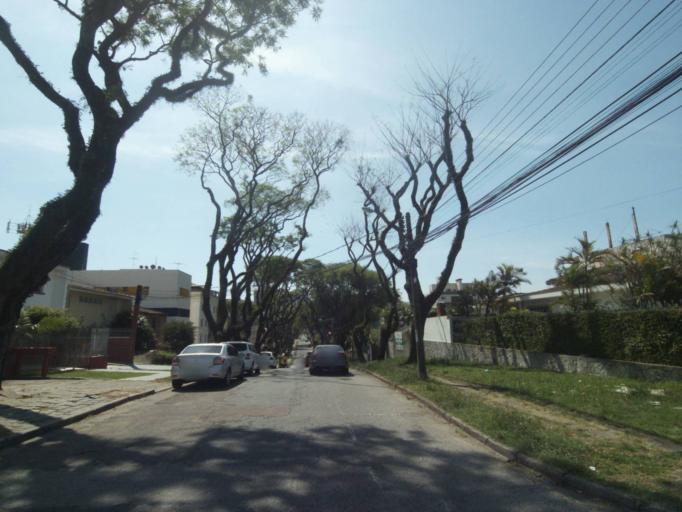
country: BR
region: Parana
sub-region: Curitiba
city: Curitiba
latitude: -25.4737
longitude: -49.2886
